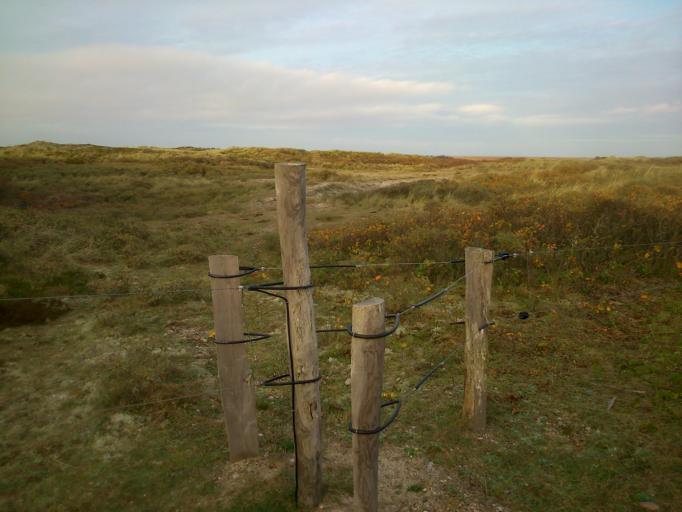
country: DK
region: Central Jutland
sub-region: Ringkobing-Skjern Kommune
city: Hvide Sande
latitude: 55.8410
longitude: 8.1685
